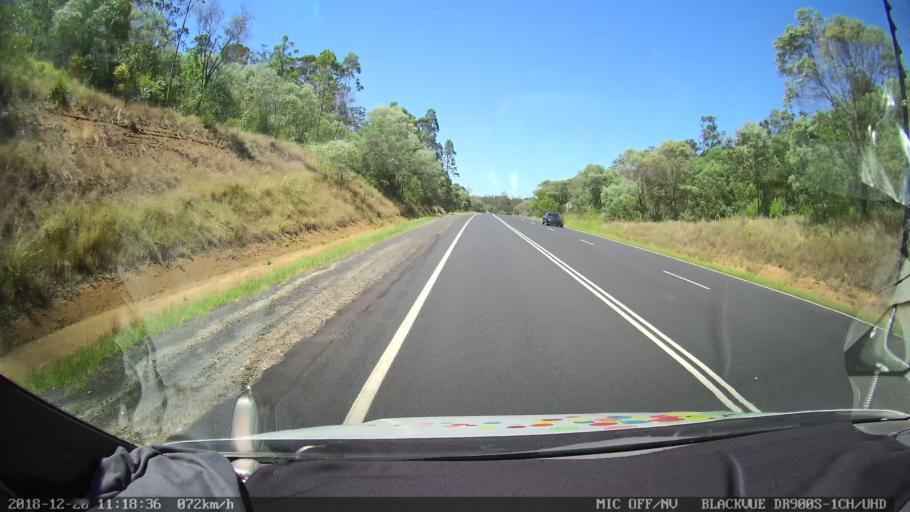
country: AU
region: New South Wales
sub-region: Richmond Valley
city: Casino
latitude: -29.0534
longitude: 153.0063
